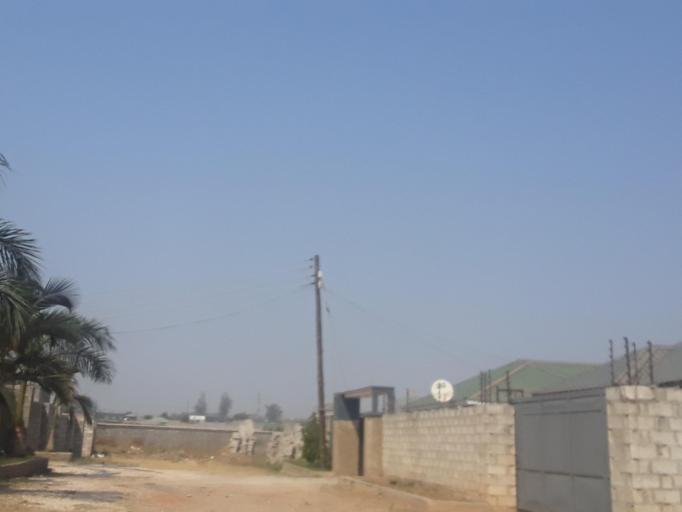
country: ZM
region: Lusaka
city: Lusaka
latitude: -15.3671
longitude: 28.2883
